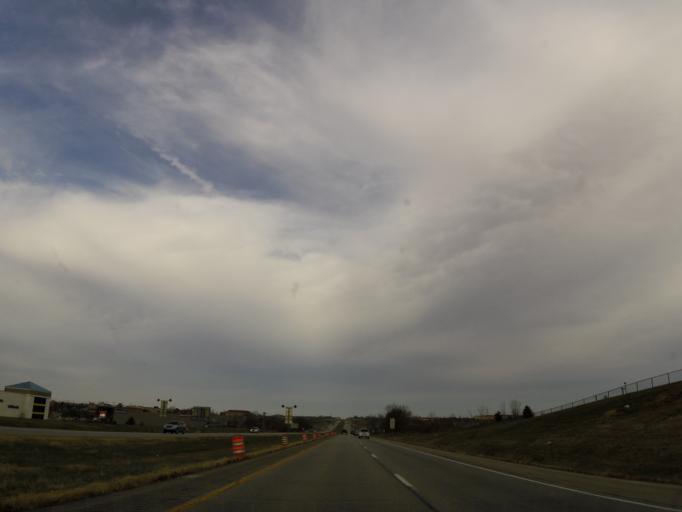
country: US
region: Iowa
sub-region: Scott County
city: Bettendorf
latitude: 41.5646
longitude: -90.5222
